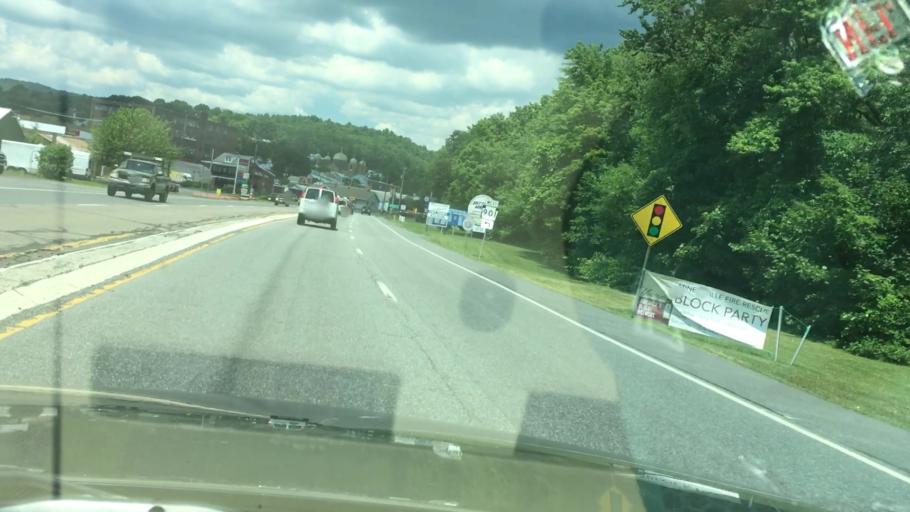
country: US
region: Pennsylvania
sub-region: Schuylkill County
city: Minersville
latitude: 40.6884
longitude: -76.2564
